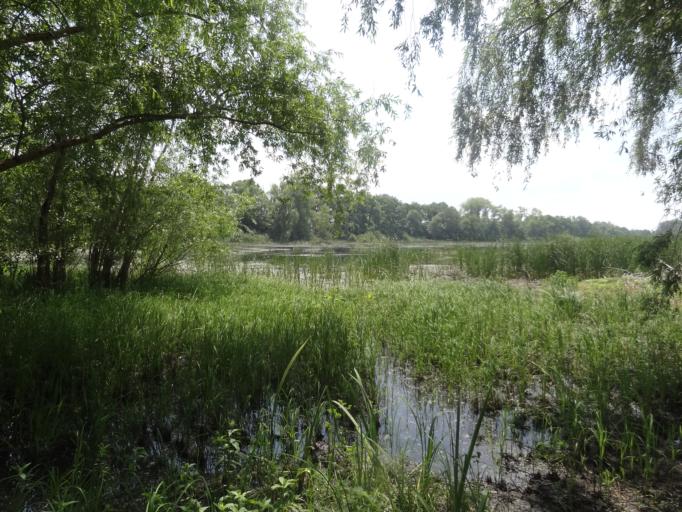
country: RU
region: Saratov
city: Engel's
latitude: 51.5454
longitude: 46.1012
